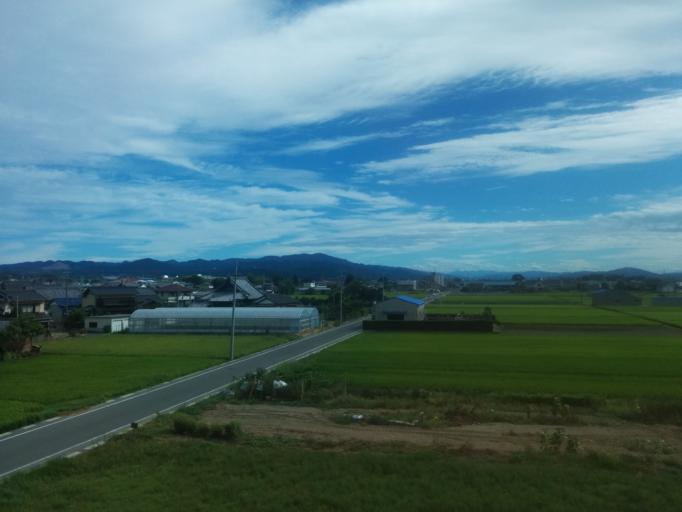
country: JP
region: Aichi
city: Kozakai-cho
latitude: 34.8046
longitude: 137.3152
